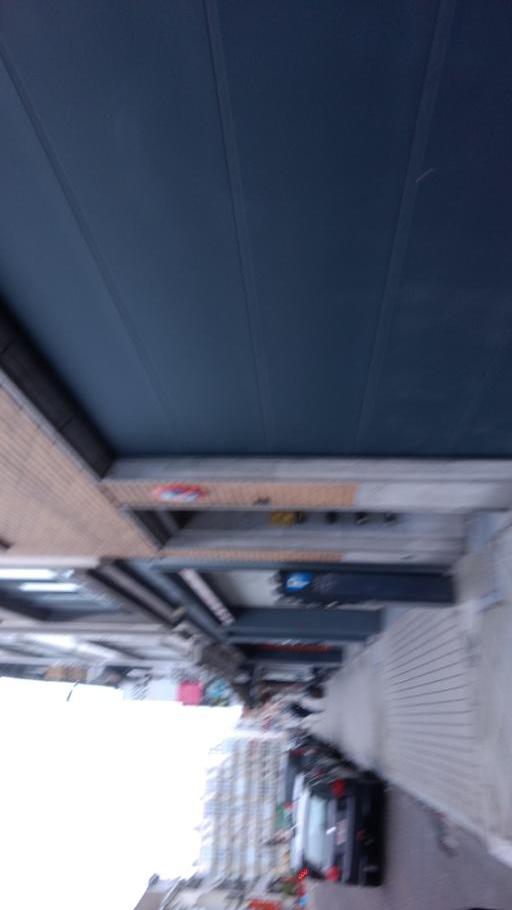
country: BE
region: Brussels Capital
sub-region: Bruxelles-Capitale
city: Brussels
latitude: 50.8190
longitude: 4.3837
